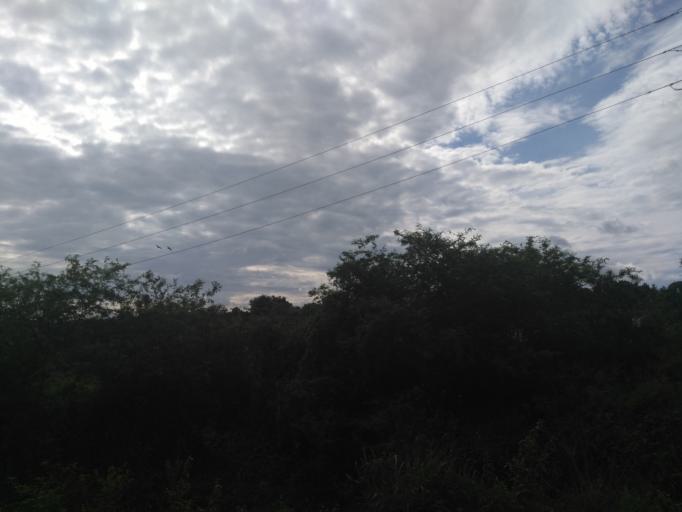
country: UG
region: Eastern Region
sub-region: Jinja District
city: Jinja
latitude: 0.4433
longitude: 33.1946
